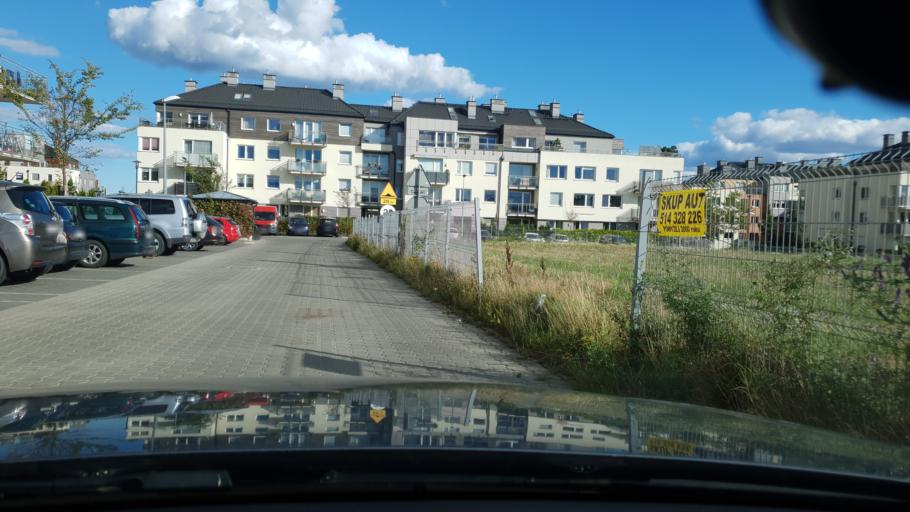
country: PL
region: Pomeranian Voivodeship
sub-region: Powiat kartuski
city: Chwaszczyno
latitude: 54.4938
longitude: 18.4374
